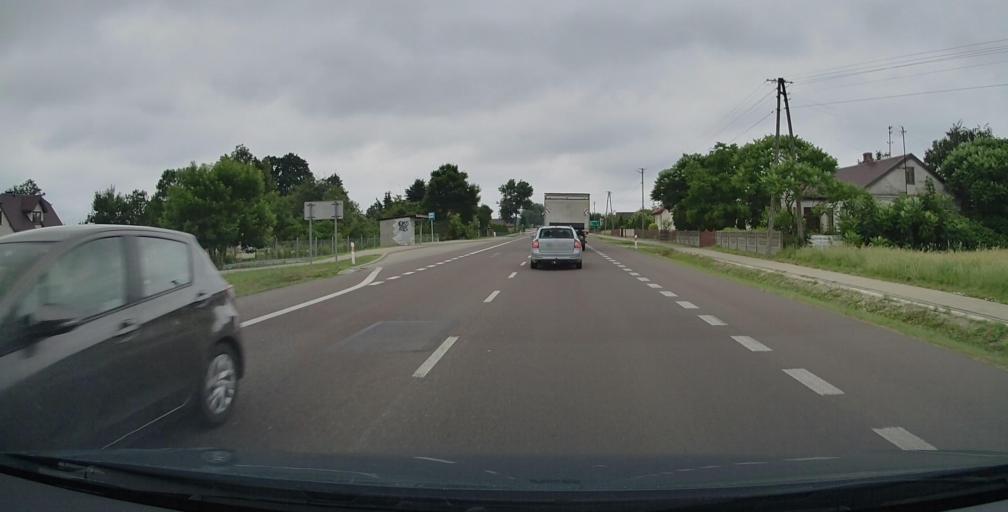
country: PL
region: Lublin Voivodeship
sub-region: Powiat bialski
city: Rzeczyca
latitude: 52.0208
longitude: 22.7227
